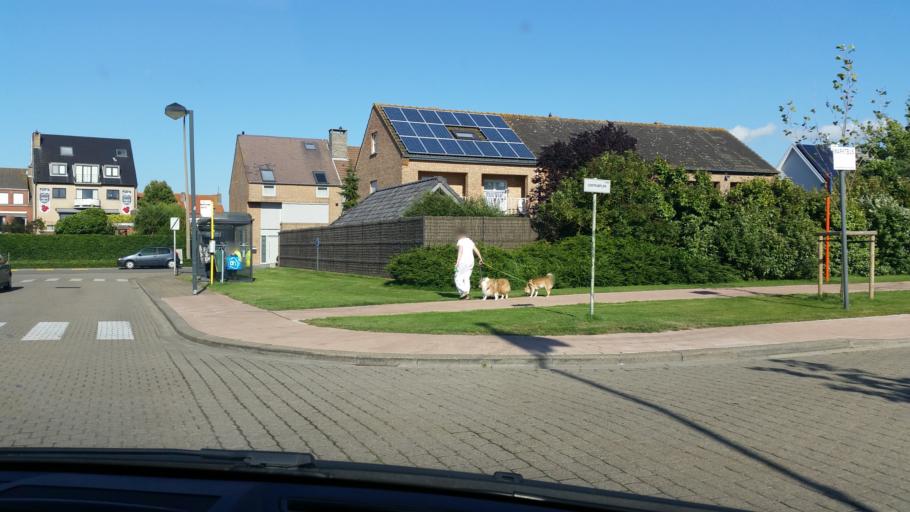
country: BE
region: Flanders
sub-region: Provincie West-Vlaanderen
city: Bredene
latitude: 51.2413
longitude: 2.9650
